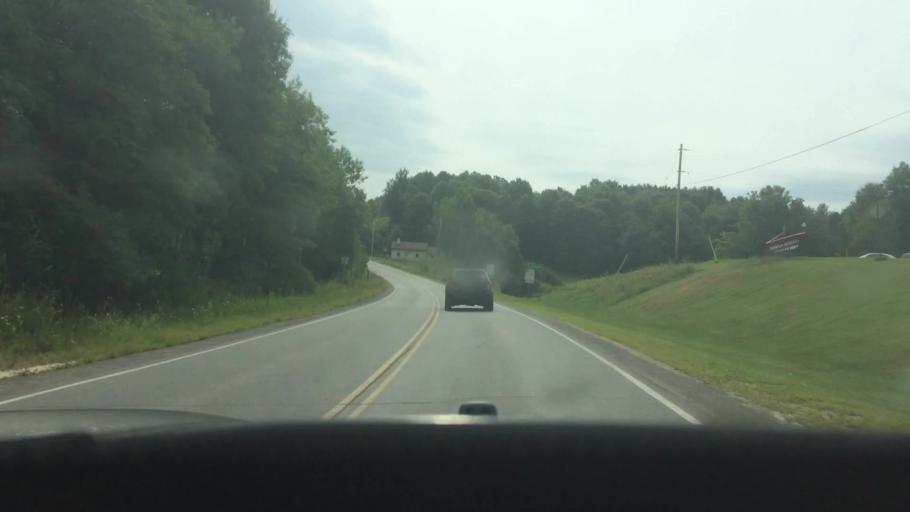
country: US
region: New York
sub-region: St. Lawrence County
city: Canton
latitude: 44.4716
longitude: -75.2374
